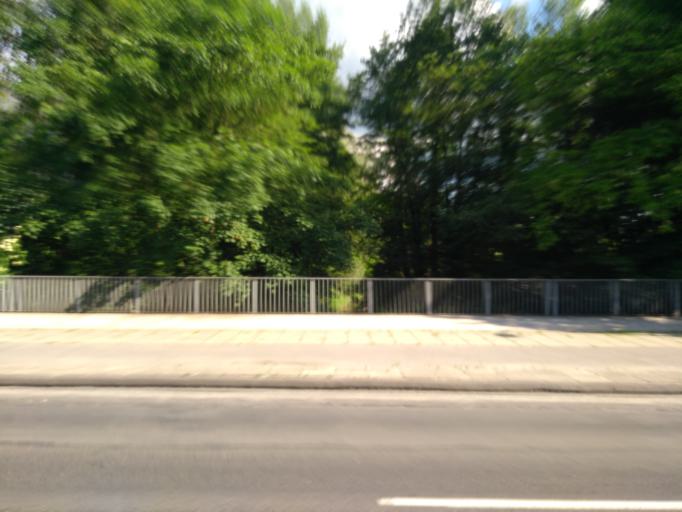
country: PL
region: Lesser Poland Voivodeship
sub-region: Powiat wielicki
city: Kokotow
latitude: 50.0772
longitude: 20.0564
